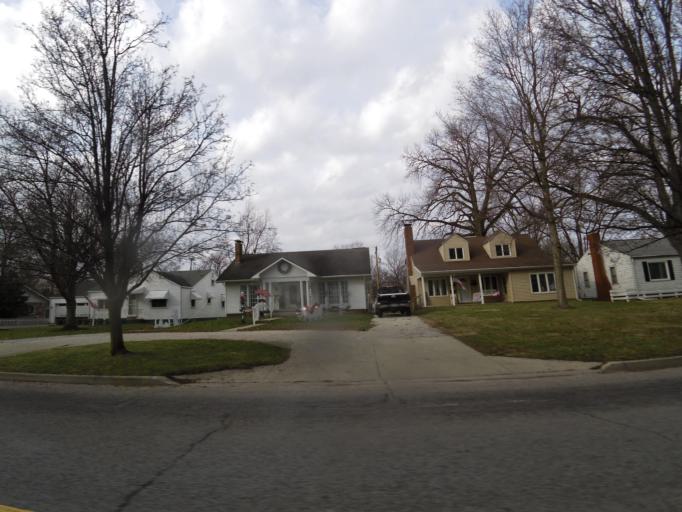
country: US
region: Illinois
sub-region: Christian County
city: Pana
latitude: 39.3775
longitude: -89.0816
